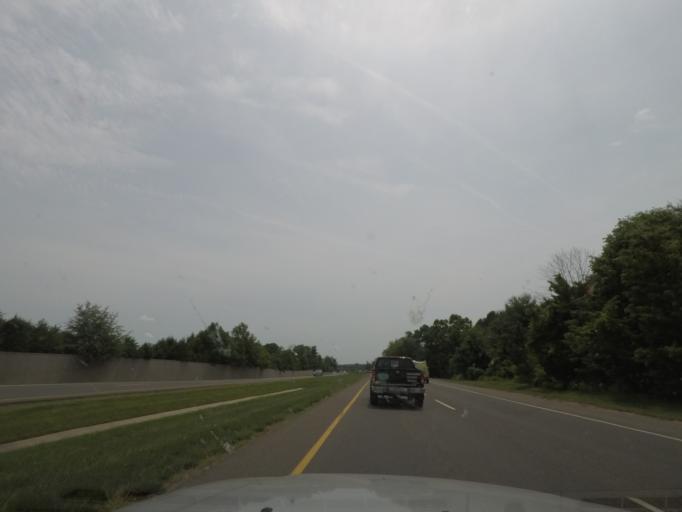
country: US
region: Virginia
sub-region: Prince William County
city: Haymarket
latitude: 38.8324
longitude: -77.6329
